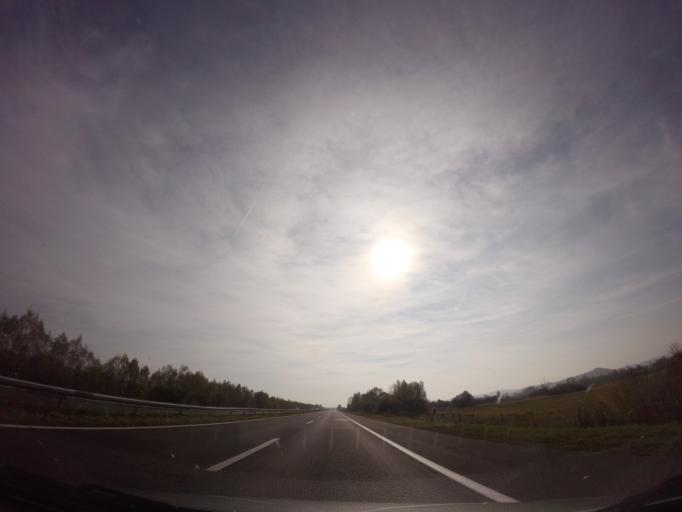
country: HR
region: Zagrebacka
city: Brckovljani
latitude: 45.9836
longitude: 16.2855
